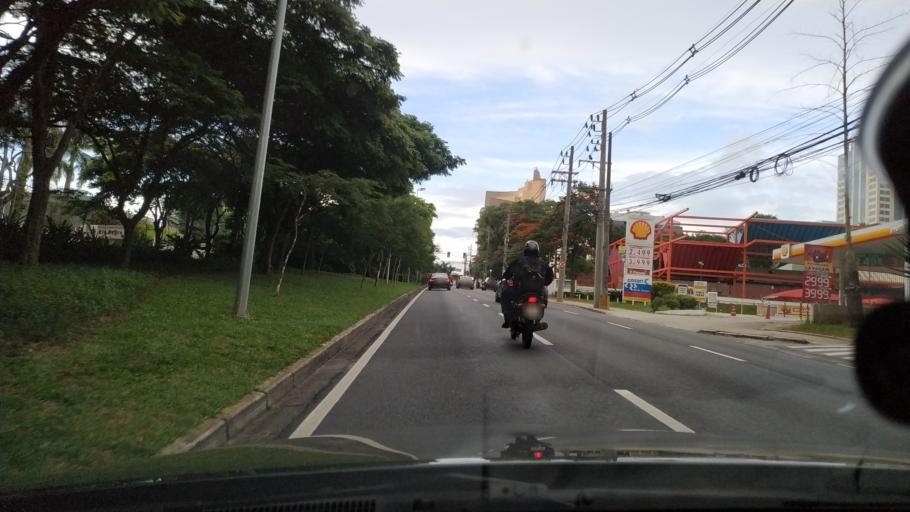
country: BR
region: Sao Paulo
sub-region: Carapicuiba
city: Carapicuiba
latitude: -23.5010
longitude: -46.8479
